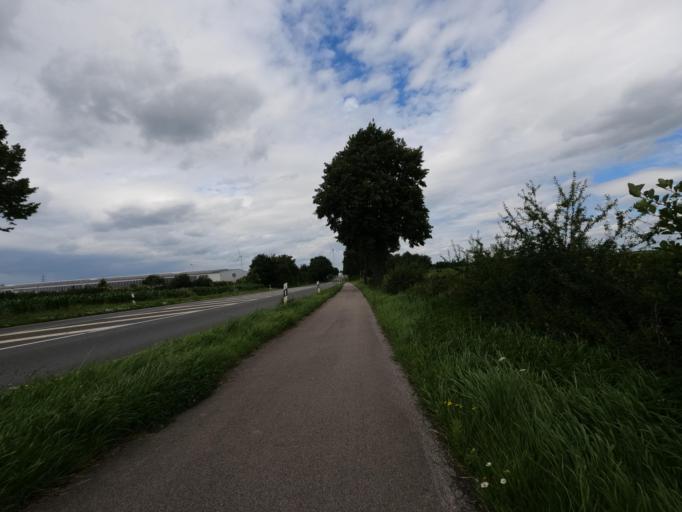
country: DE
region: North Rhine-Westphalia
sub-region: Regierungsbezirk Koln
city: Ubach-Palenberg
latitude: 50.9238
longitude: 6.1367
